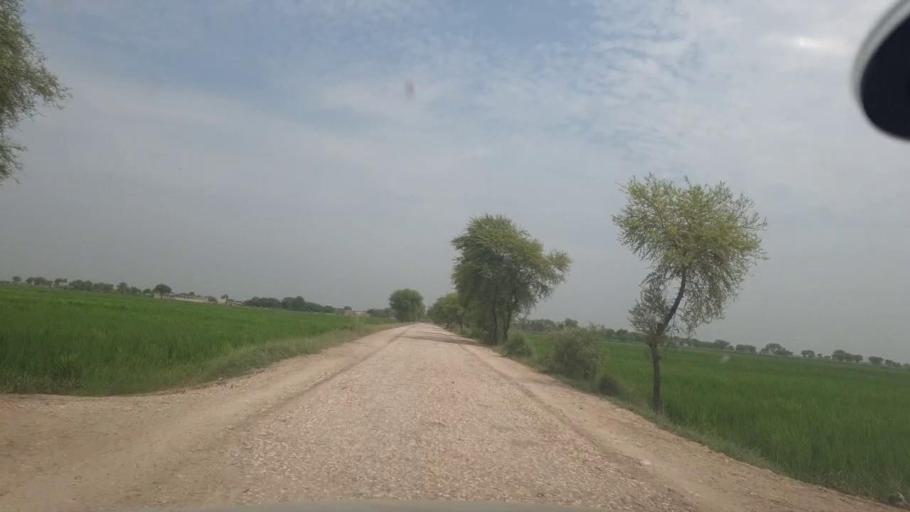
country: PK
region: Sindh
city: Jacobabad
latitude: 28.2475
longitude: 68.5421
